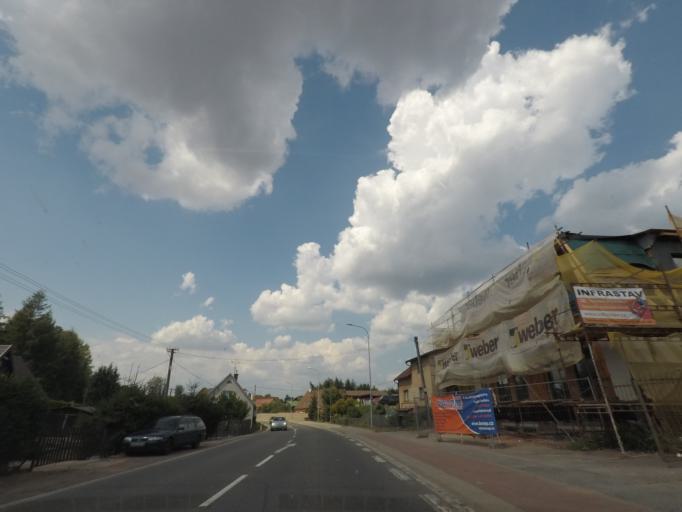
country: CZ
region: Kralovehradecky
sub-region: Okres Trutnov
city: Trutnov
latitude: 50.5590
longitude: 15.8817
